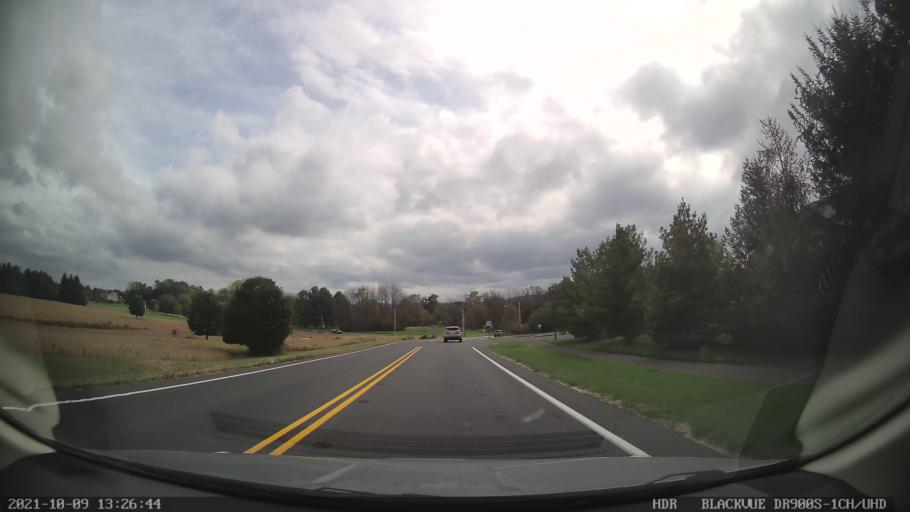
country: US
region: Pennsylvania
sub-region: Lehigh County
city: Ancient Oaks
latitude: 40.5460
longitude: -75.5789
